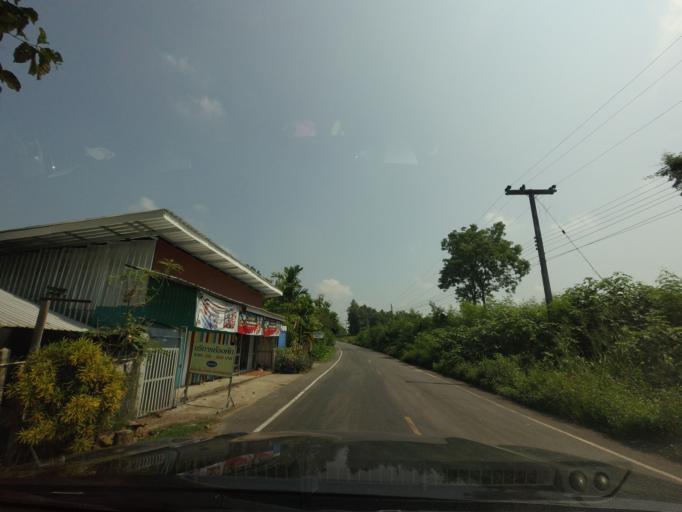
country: TH
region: Nan
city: Nan
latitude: 18.8349
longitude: 100.7777
